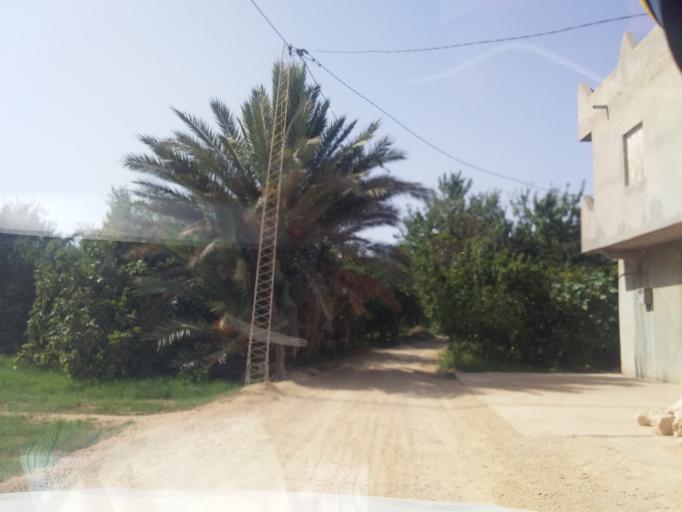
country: TN
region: Qabis
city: Gabes
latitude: 33.6270
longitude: 10.2917
